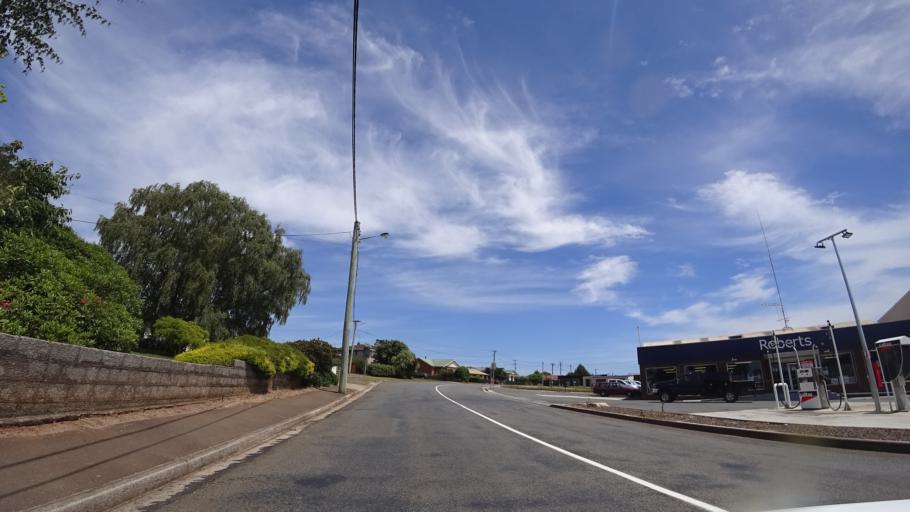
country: AU
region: Tasmania
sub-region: Dorset
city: Scottsdale
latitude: -41.1585
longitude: 147.5095
